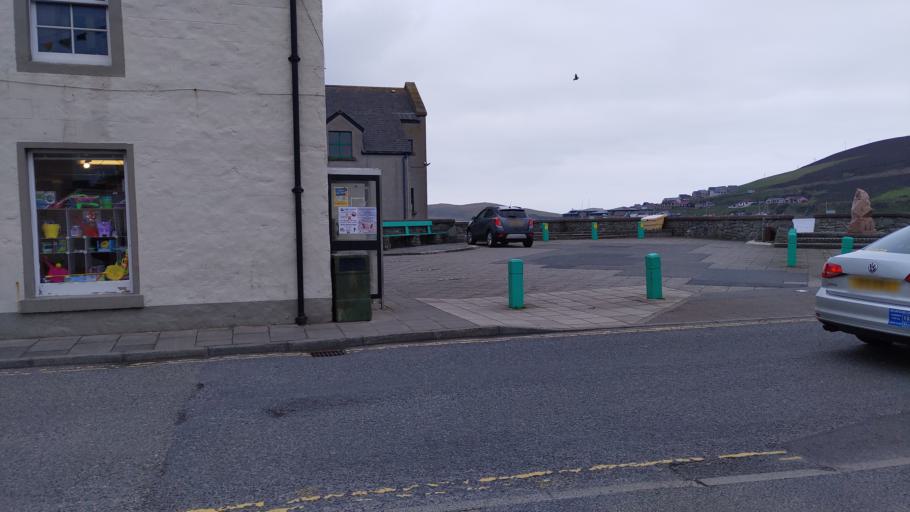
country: GB
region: Scotland
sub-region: Shetland Islands
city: Lerwick
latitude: 60.1373
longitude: -1.2765
